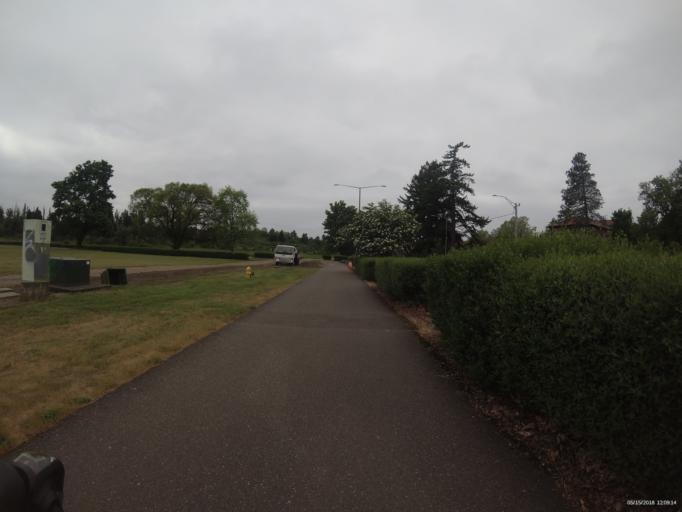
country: US
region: Washington
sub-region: Pierce County
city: Steilacoom
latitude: 47.1772
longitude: -122.5639
